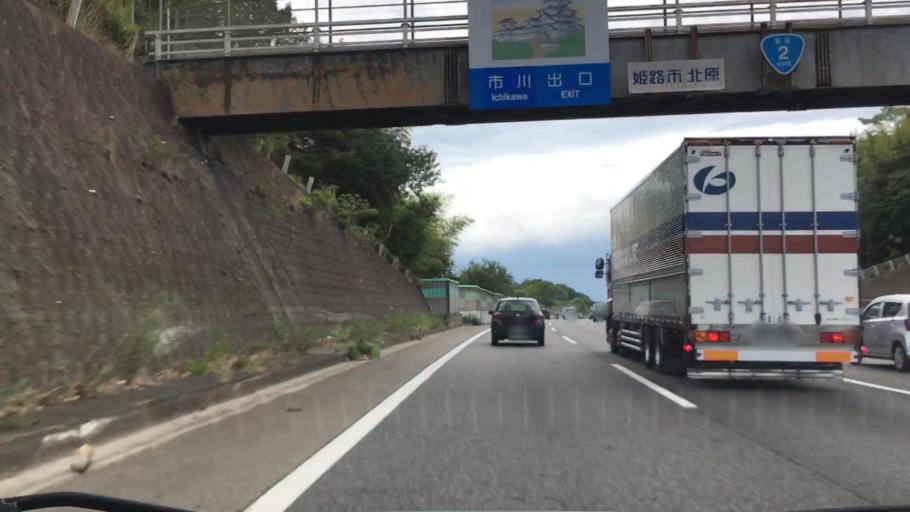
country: JP
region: Hyogo
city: Shirahamacho-usazakiminami
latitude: 34.8003
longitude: 134.7103
